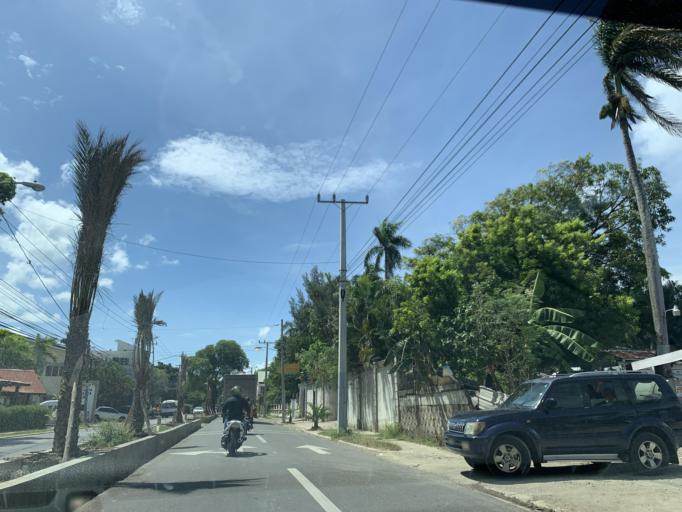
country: DO
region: Puerto Plata
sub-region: Puerto Plata
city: Puerto Plata
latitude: 19.7892
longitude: -70.6784
